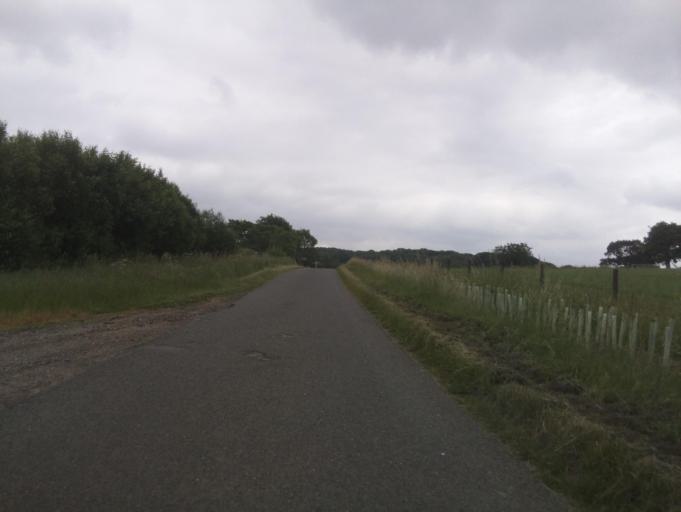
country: GB
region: England
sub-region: District of Rutland
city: Langham
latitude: 52.6752
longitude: -0.7917
